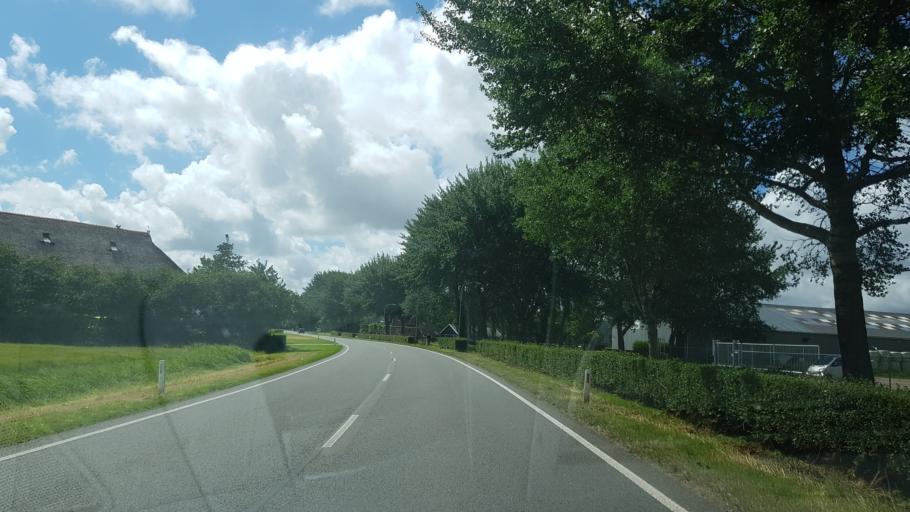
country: NL
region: Groningen
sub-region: Gemeente Winsum
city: Winsum
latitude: 53.3992
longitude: 6.5722
